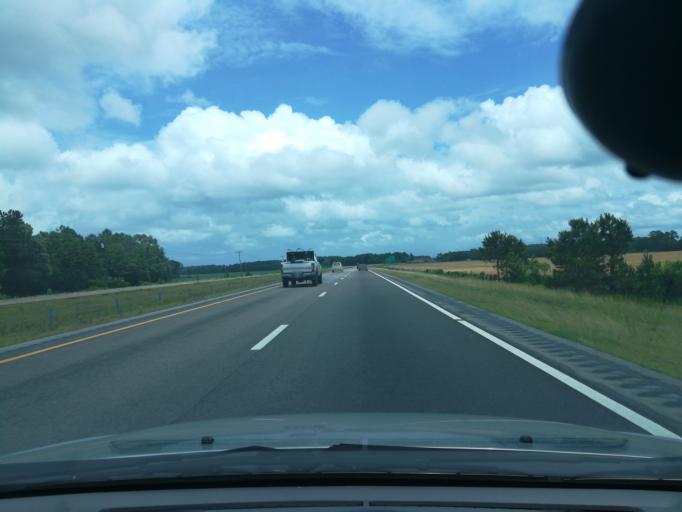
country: US
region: North Carolina
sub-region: Tyrrell County
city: Columbia
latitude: 35.8970
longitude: -76.3416
